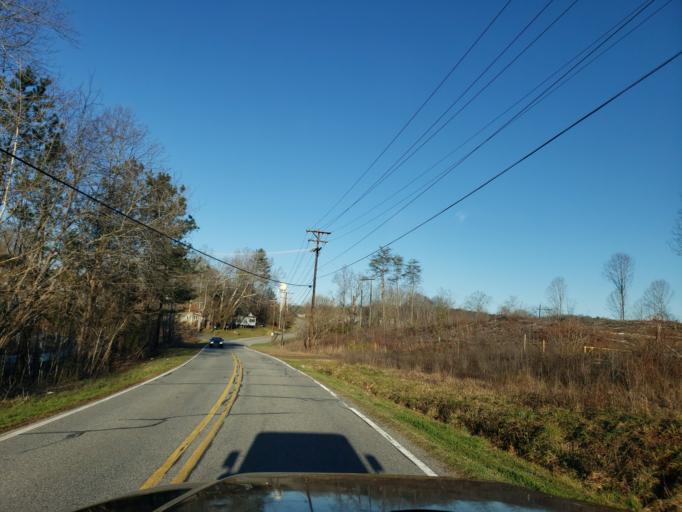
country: US
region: North Carolina
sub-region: Cleveland County
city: Shelby
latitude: 35.4106
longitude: -81.5668
